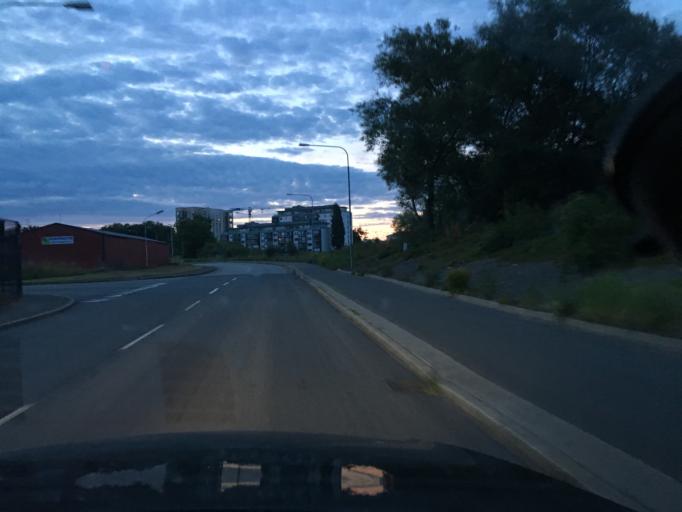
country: SE
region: Skane
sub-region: Kristianstads Kommun
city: Kristianstad
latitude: 56.0224
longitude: 14.1540
